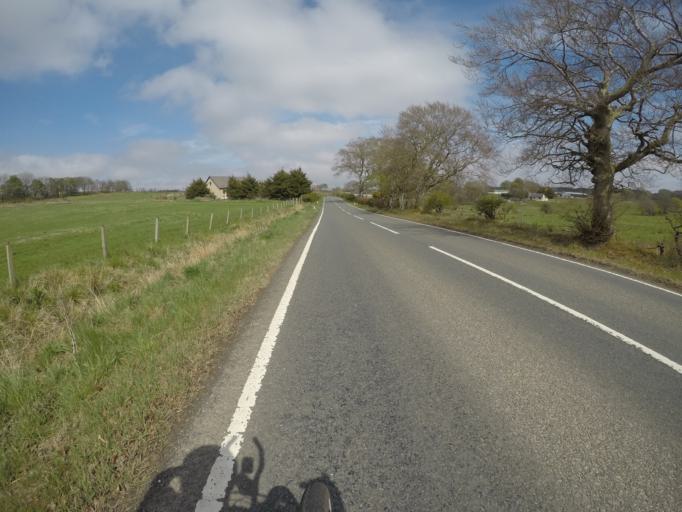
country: GB
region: Scotland
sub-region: East Ayrshire
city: Stewarton
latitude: 55.7092
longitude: -4.4579
